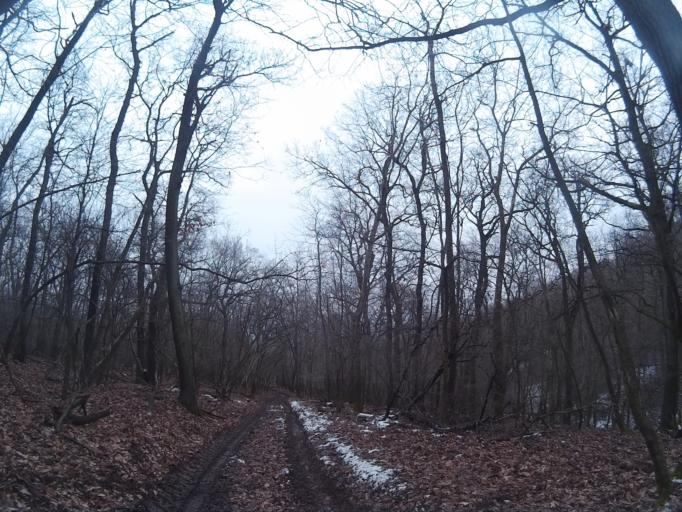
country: HU
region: Komarom-Esztergom
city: Tarjan
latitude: 47.5723
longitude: 18.5400
